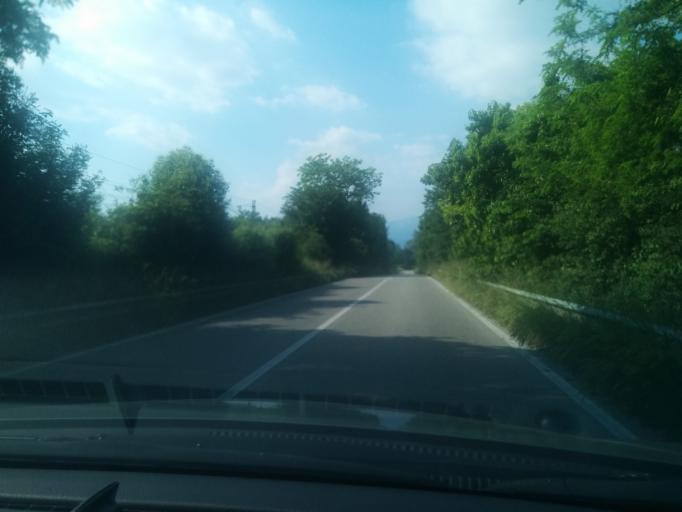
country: IT
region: Friuli Venezia Giulia
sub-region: Provincia di Udine
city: Reana del Rojale
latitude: 46.1360
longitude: 13.2436
